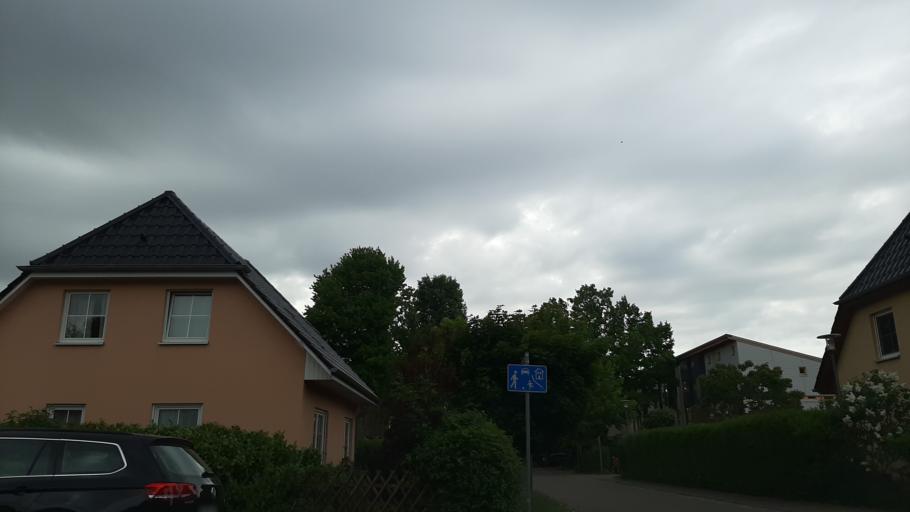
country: DE
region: Brandenburg
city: Hennigsdorf
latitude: 52.6443
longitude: 13.1873
